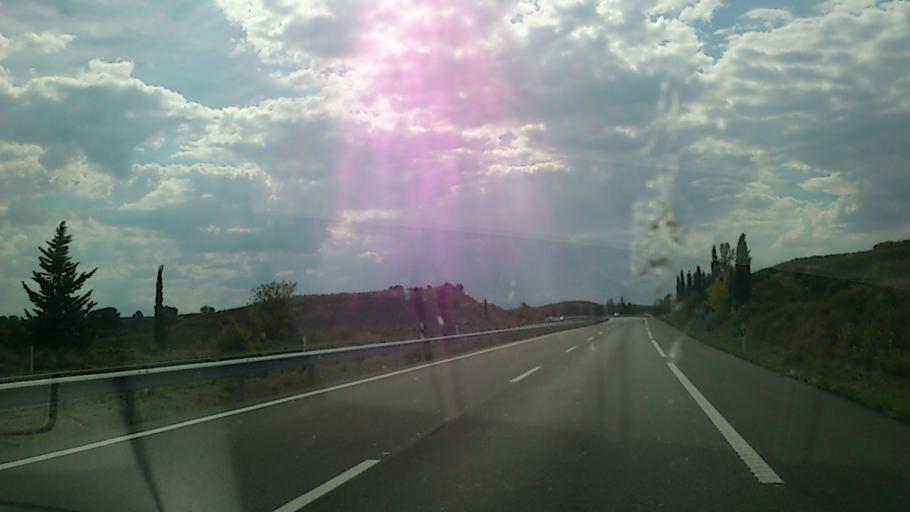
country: ES
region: La Rioja
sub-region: Provincia de La Rioja
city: Haro
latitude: 42.5944
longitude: -2.8603
